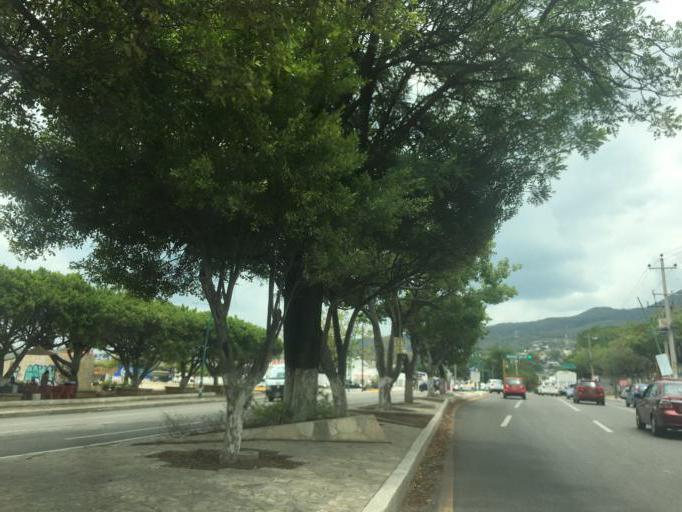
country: MX
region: Chiapas
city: Tuxtla Gutierrez
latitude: 16.7513
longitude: -93.1417
